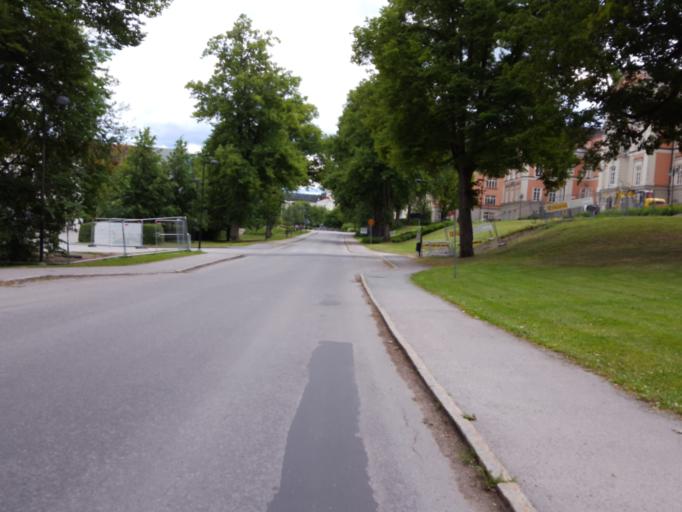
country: SE
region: Uppsala
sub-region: Uppsala Kommun
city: Uppsala
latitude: 59.8526
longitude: 17.6385
